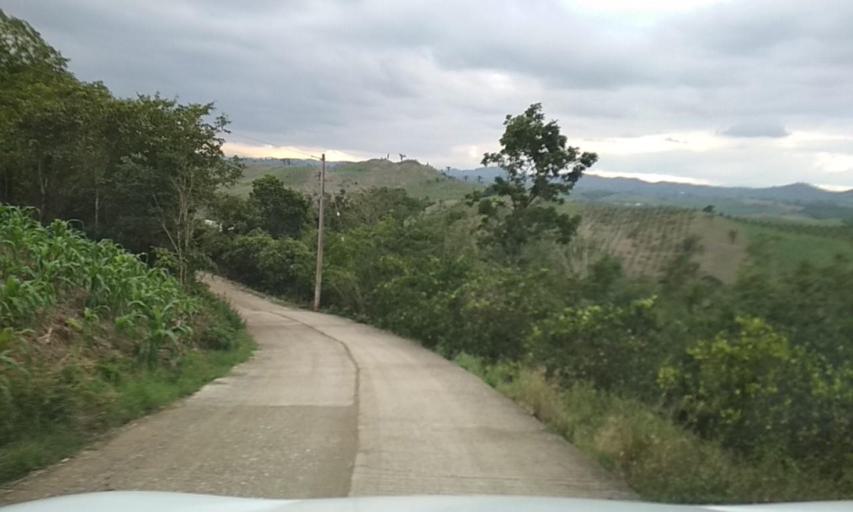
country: MX
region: Veracruz
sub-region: Coatzintla
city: Manuel Maria Contreras
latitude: 20.3814
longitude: -97.4439
